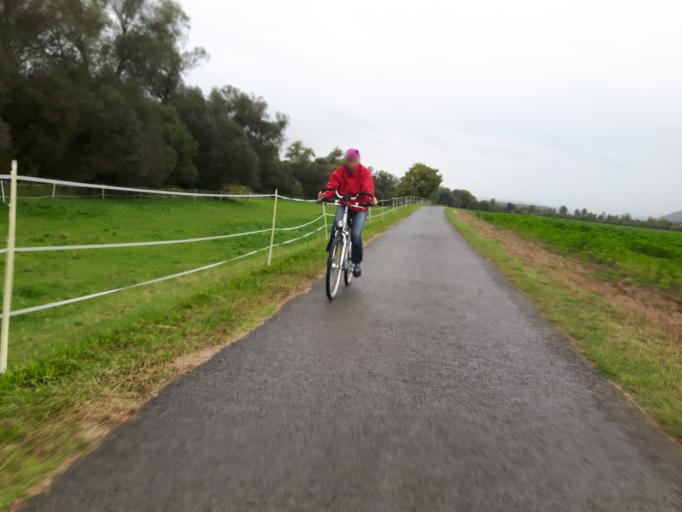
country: DE
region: Bavaria
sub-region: Regierungsbezirk Unterfranken
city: Himmelstadt
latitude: 49.9376
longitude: 9.8034
